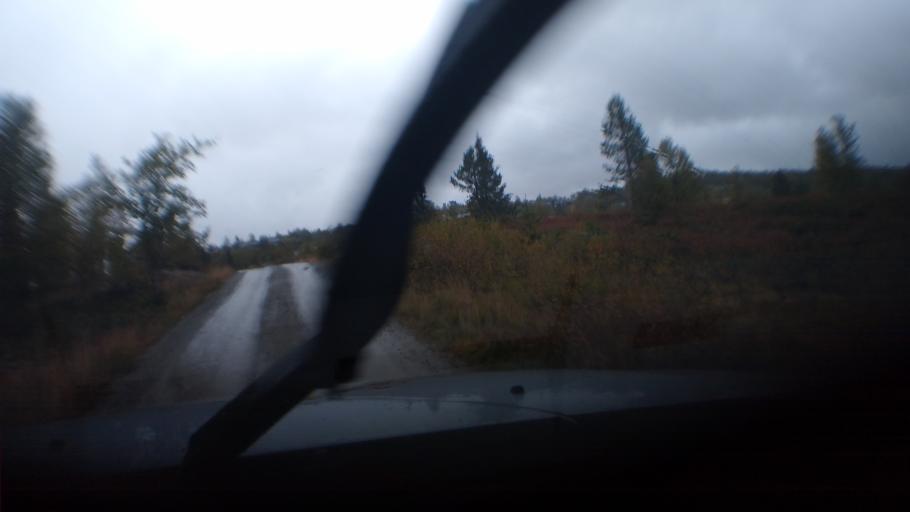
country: NO
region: Oppland
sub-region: Ringebu
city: Ringebu
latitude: 61.6499
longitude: 10.0957
